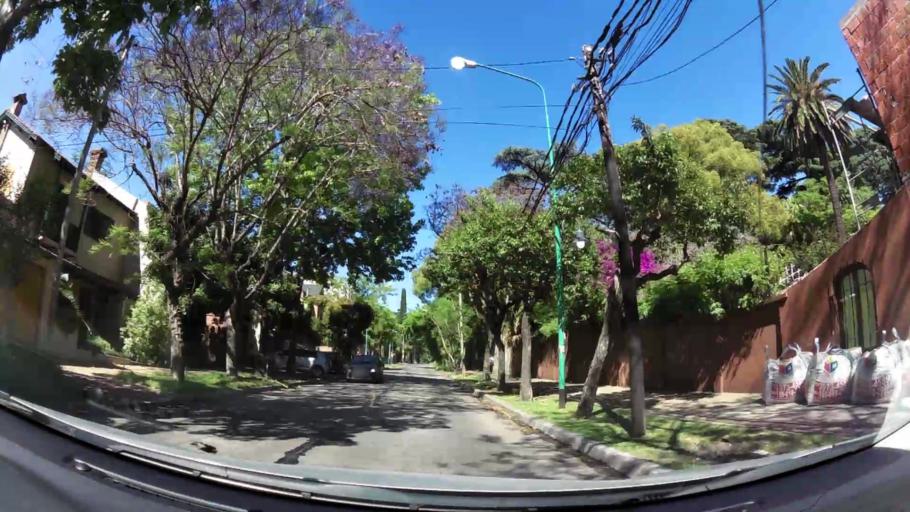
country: AR
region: Buenos Aires
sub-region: Partido de Vicente Lopez
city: Olivos
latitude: -34.5326
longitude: -58.4713
